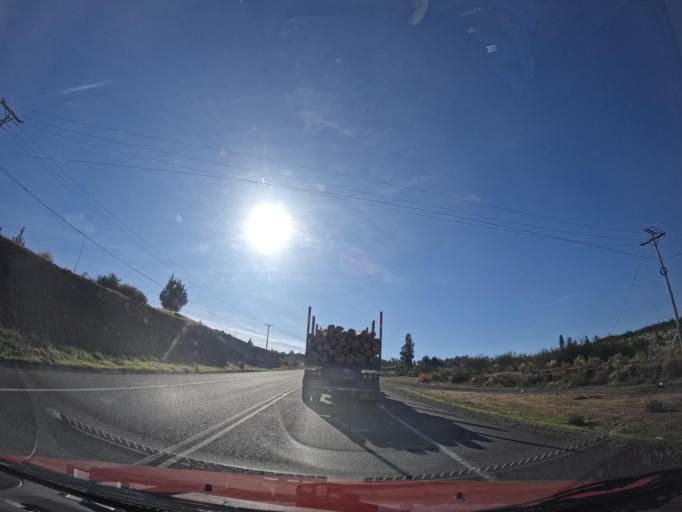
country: CL
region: Maule
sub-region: Provincia de Cauquenes
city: Cauquenes
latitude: -35.9366
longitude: -72.1958
